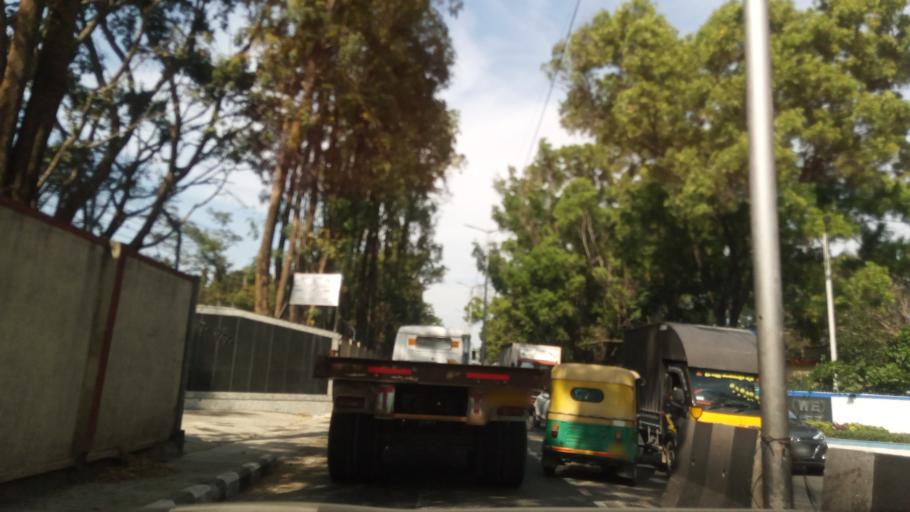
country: IN
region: Karnataka
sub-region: Bangalore Urban
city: Bangalore
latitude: 13.0367
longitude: 77.5416
